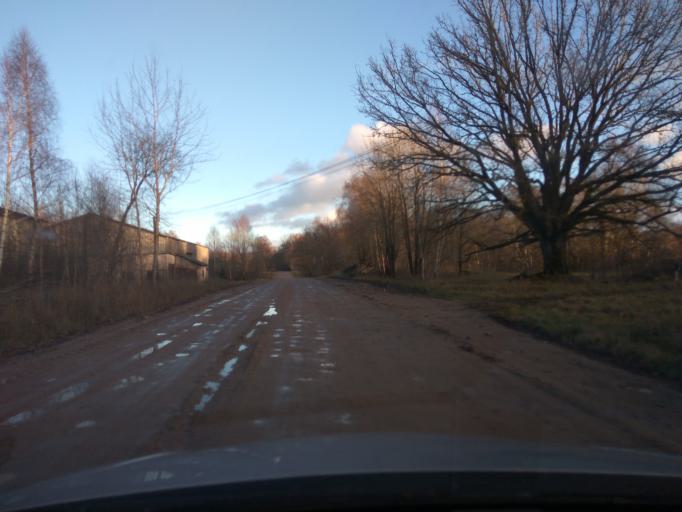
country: LV
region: Aizpute
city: Aizpute
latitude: 56.8336
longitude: 21.7868
